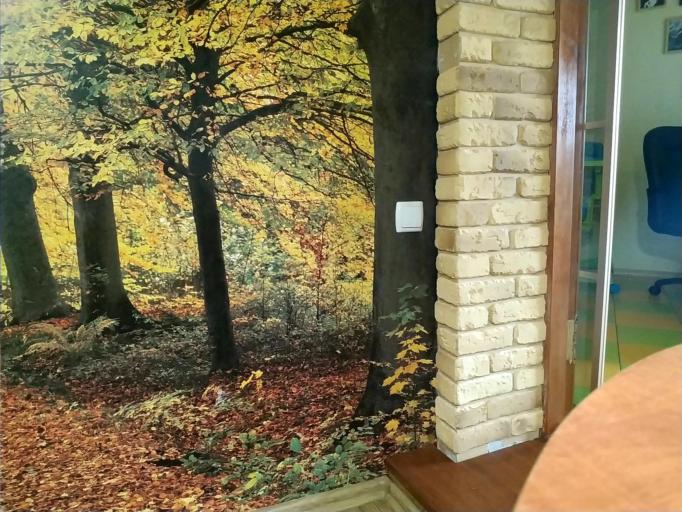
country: RU
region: Smolensk
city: Dorogobuzh
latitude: 54.9663
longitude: 33.2790
